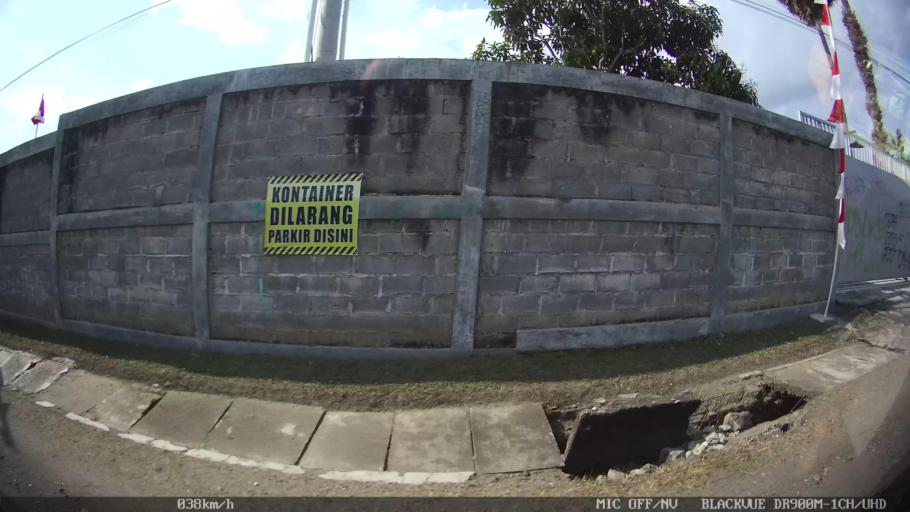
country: ID
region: Daerah Istimewa Yogyakarta
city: Kasihan
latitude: -7.8379
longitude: 110.3174
